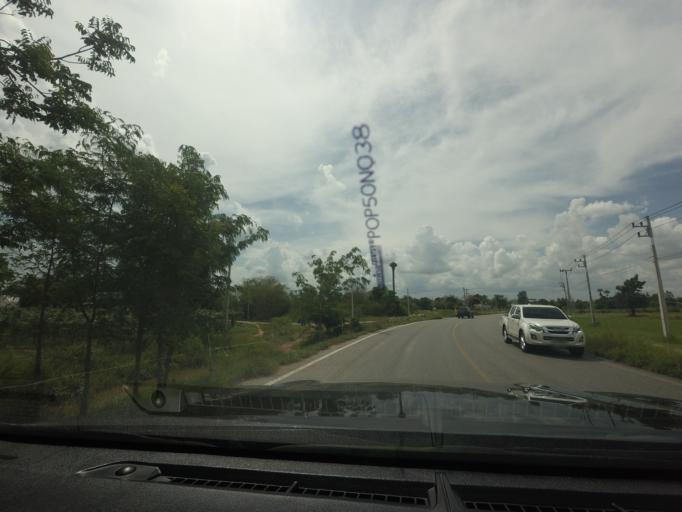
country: TH
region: Kanchanaburi
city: Phanom Thuan
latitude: 14.1692
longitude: 99.6035
